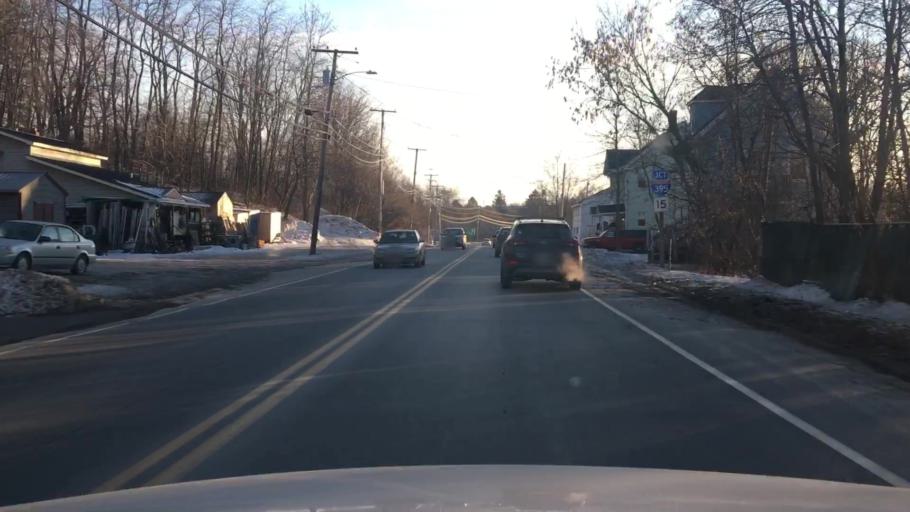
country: US
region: Maine
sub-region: Penobscot County
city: Brewer
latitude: 44.7878
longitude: -68.7706
